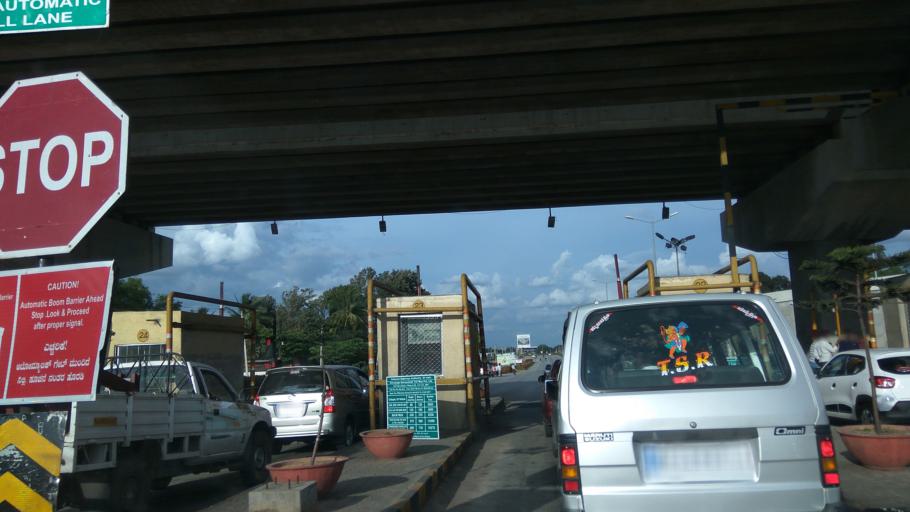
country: IN
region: Karnataka
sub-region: Bangalore Rural
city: Devanhalli
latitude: 13.2010
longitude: 77.6610
